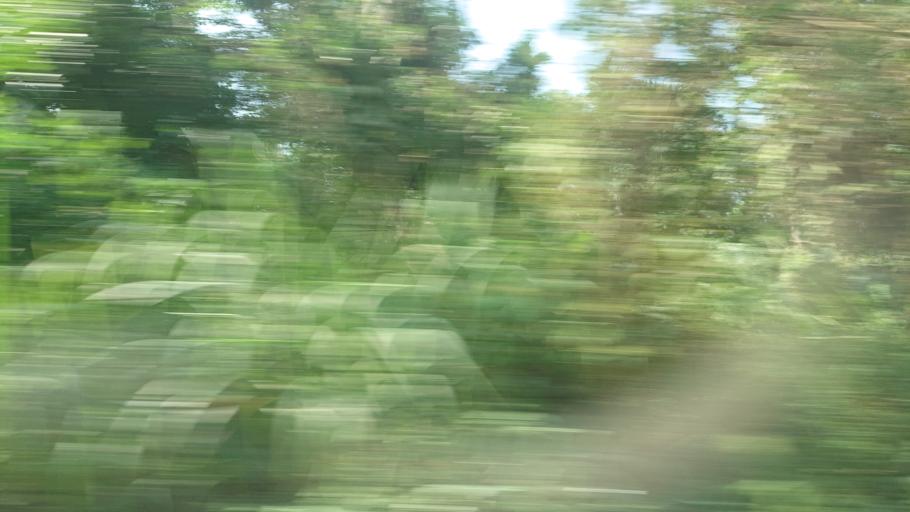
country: TW
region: Taiwan
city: Lugu
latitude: 23.7218
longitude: 120.6693
